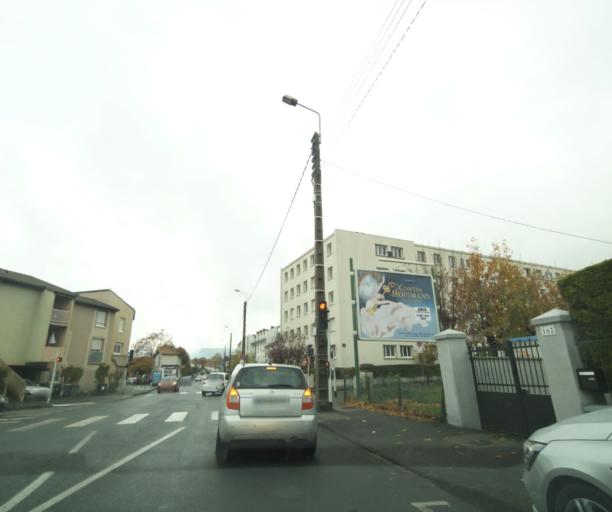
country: FR
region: Auvergne
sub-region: Departement du Puy-de-Dome
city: Aubiere
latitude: 45.7616
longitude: 3.1001
